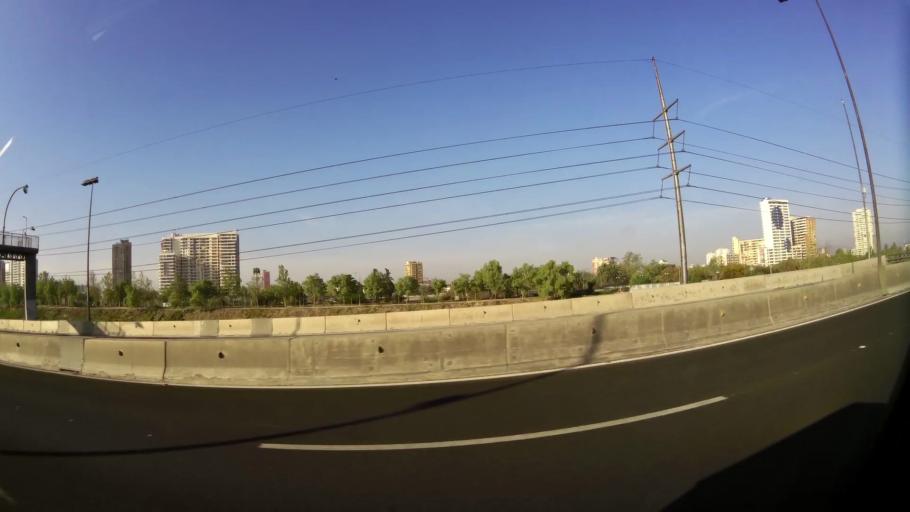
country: CL
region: Santiago Metropolitan
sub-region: Provincia de Santiago
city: Santiago
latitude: -33.4262
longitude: -70.6706
